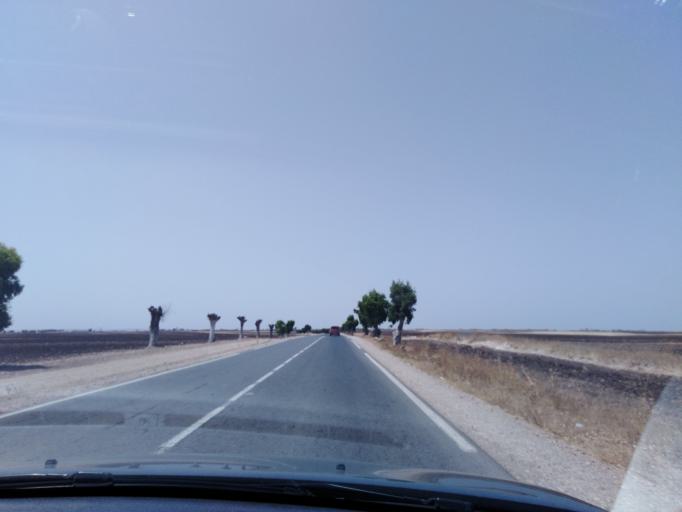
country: MA
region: Doukkala-Abda
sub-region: Safi
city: Youssoufia
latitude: 32.3884
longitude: -8.8232
